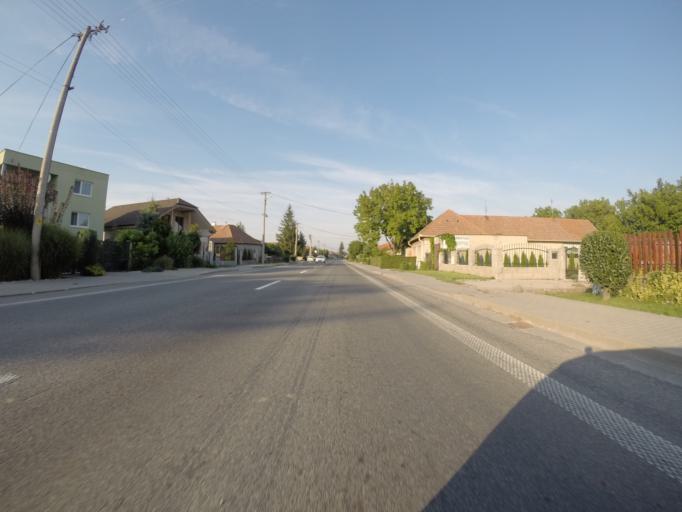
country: SK
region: Nitriansky
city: Banovce nad Bebravou
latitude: 48.6036
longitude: 18.2216
